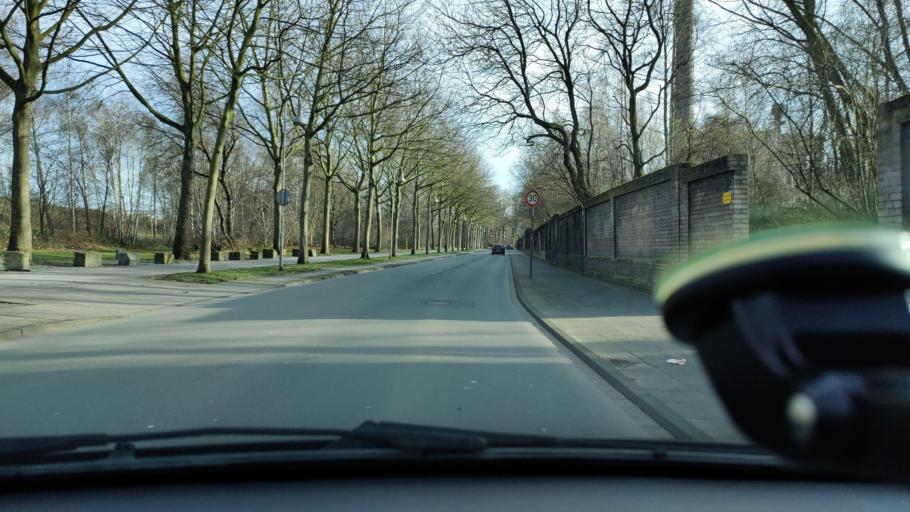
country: DE
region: North Rhine-Westphalia
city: Meiderich
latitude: 51.4838
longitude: 6.7816
